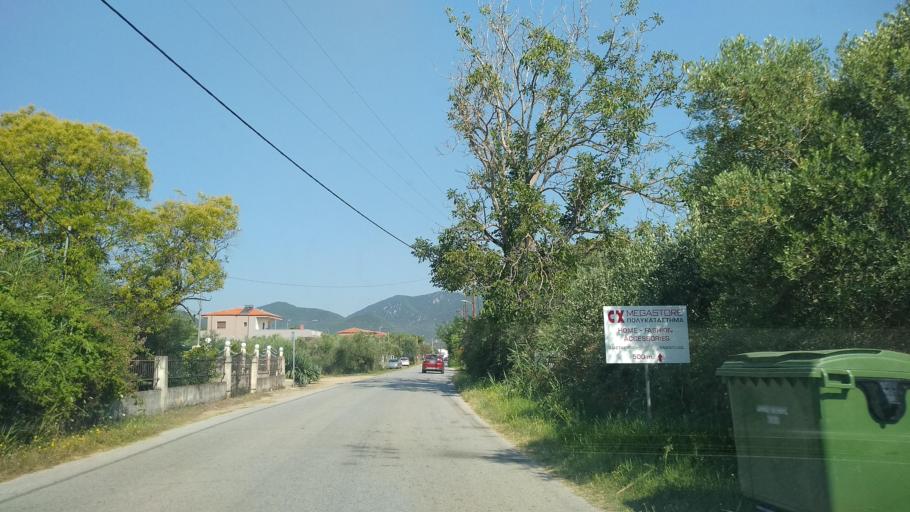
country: GR
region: Central Macedonia
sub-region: Nomos Thessalonikis
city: Nea Vrasna
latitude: 40.6903
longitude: 23.6867
